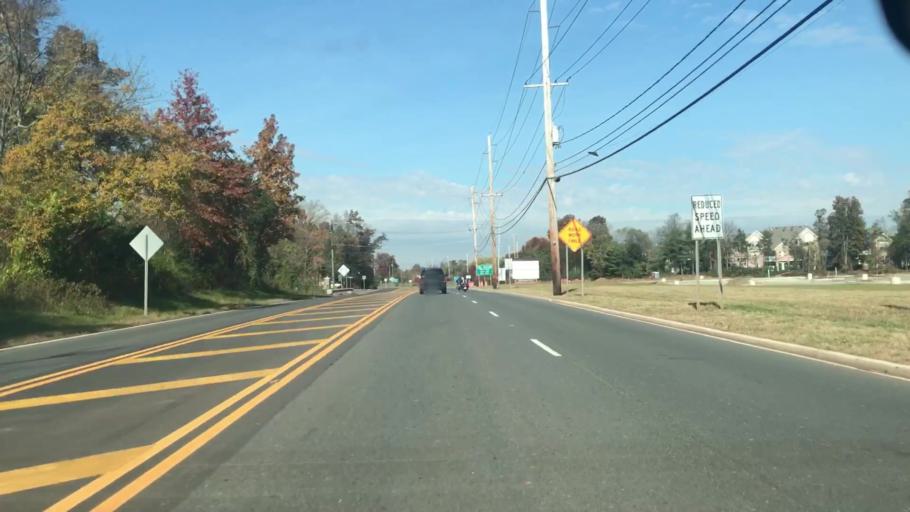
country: US
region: New Jersey
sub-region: Somerset County
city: Bloomingdale
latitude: 40.4605
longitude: -74.6586
